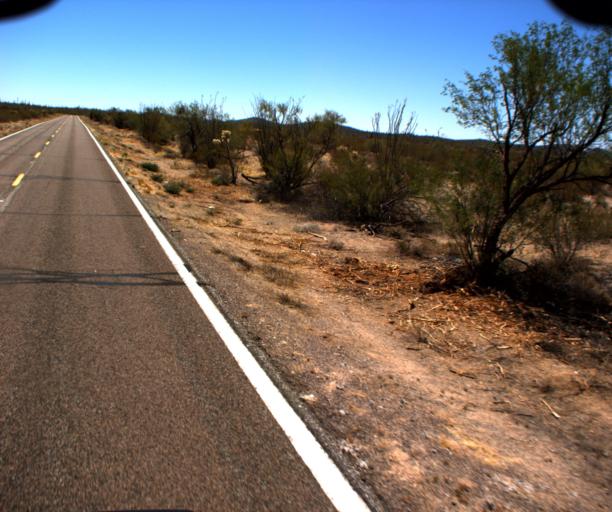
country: US
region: Arizona
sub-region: Pima County
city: Ajo
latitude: 32.2146
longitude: -112.6369
